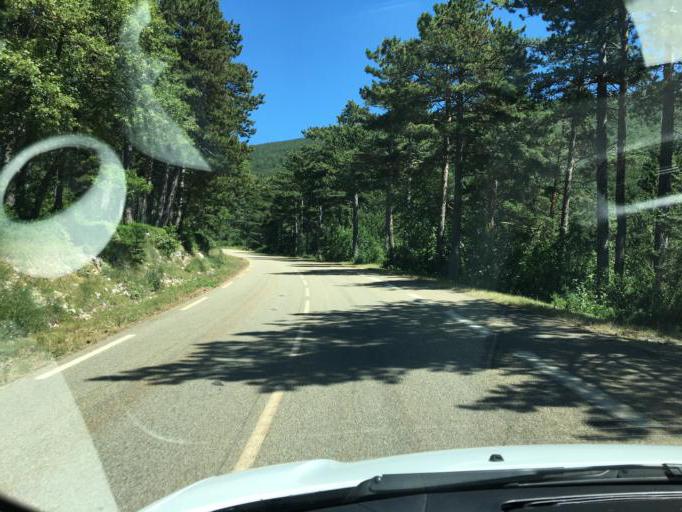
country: FR
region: Provence-Alpes-Cote d'Azur
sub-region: Departement du Vaucluse
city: Bedoin
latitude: 44.1733
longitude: 5.2183
